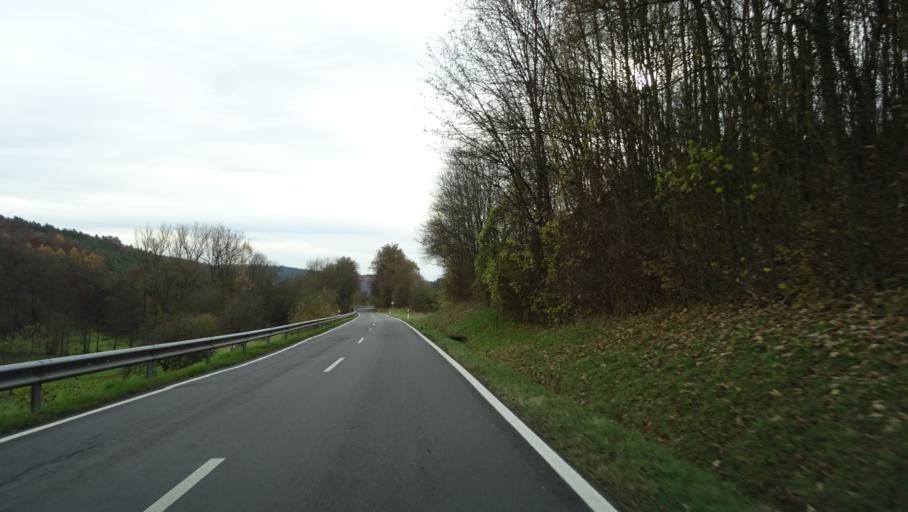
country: DE
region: Baden-Wuerttemberg
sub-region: Karlsruhe Region
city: Mosbach
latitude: 49.3648
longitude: 9.1265
